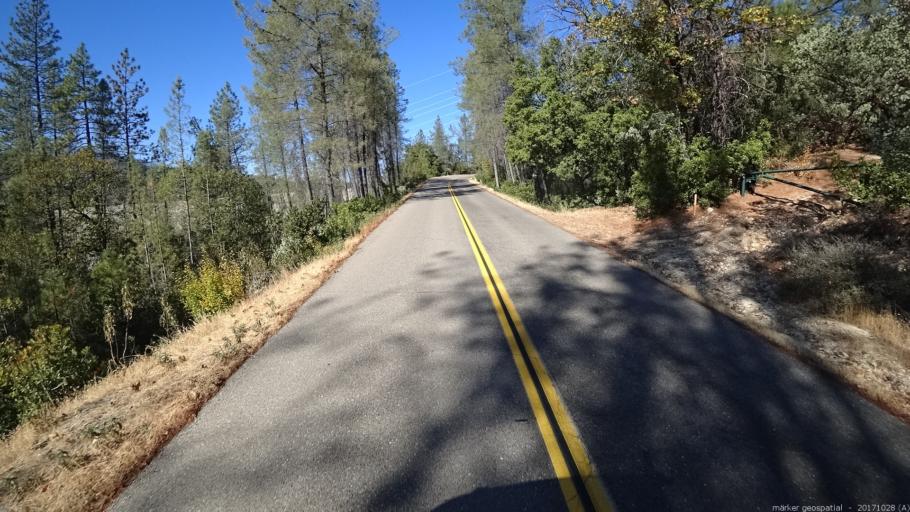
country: US
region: California
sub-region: Shasta County
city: Shasta
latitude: 40.5981
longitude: -122.5346
